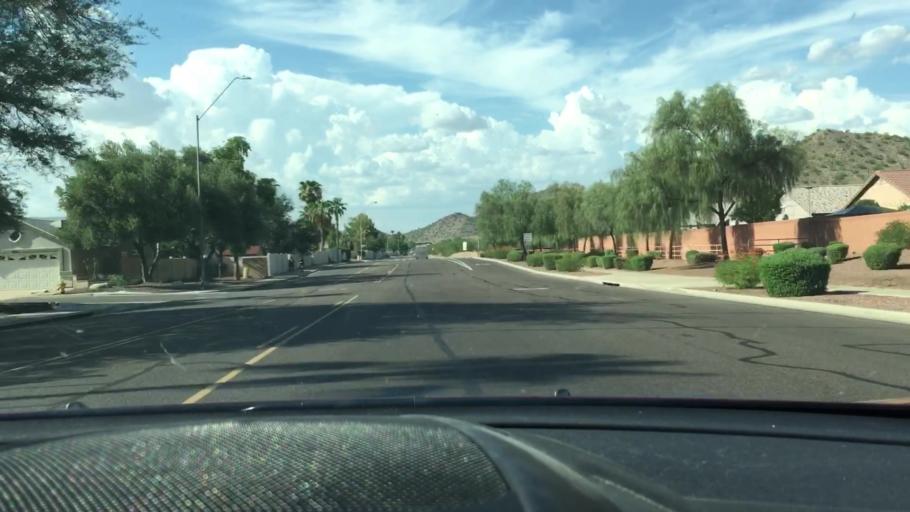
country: US
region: Arizona
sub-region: Maricopa County
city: Paradise Valley
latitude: 33.6570
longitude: -112.0485
